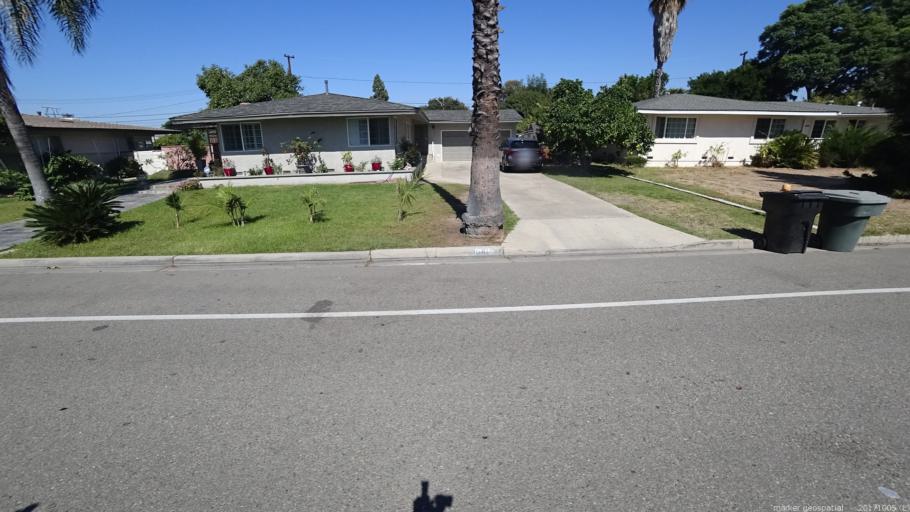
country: US
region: California
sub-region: Orange County
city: Stanton
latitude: 33.7951
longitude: -117.9661
